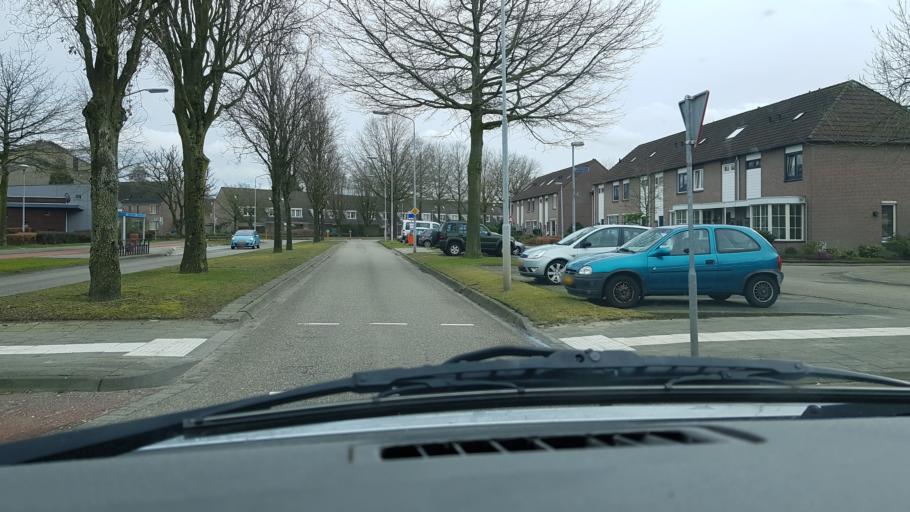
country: NL
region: North Brabant
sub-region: Gemeente Veldhoven
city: Veldhoven
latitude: 51.4272
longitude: 5.3913
